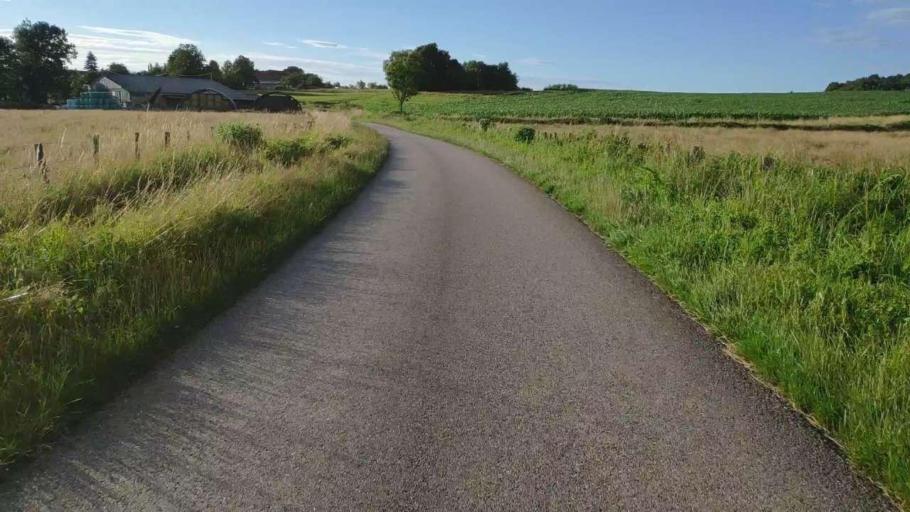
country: FR
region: Franche-Comte
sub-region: Departement du Jura
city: Bletterans
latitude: 46.7776
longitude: 5.4960
